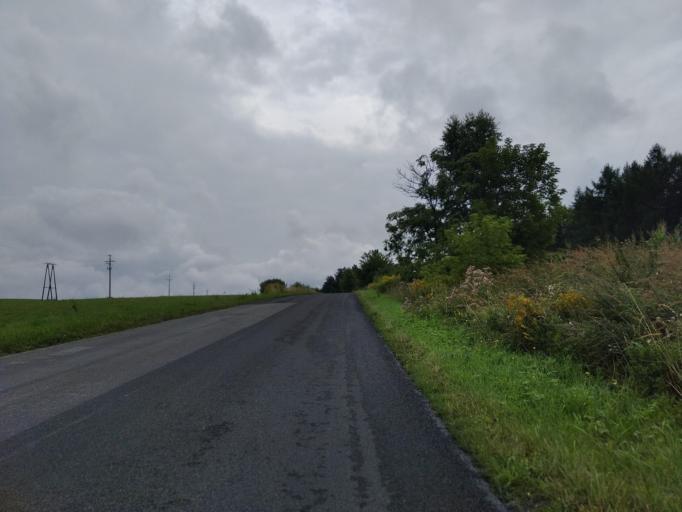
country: PL
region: Subcarpathian Voivodeship
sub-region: Powiat rzeszowski
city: Dynow
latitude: 49.7209
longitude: 22.3172
